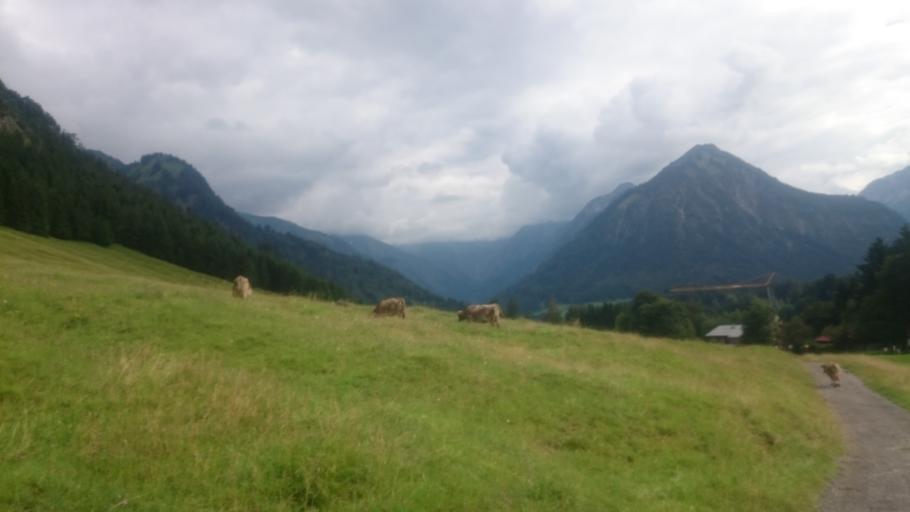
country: DE
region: Bavaria
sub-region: Swabia
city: Oberstdorf
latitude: 47.4011
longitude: 10.2945
